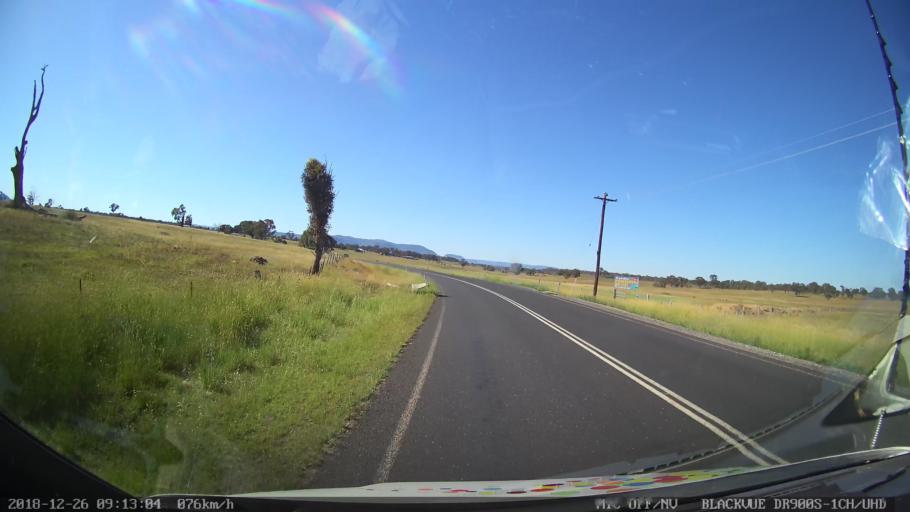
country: AU
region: New South Wales
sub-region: Mid-Western Regional
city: Kandos
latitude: -32.7638
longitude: 149.9780
